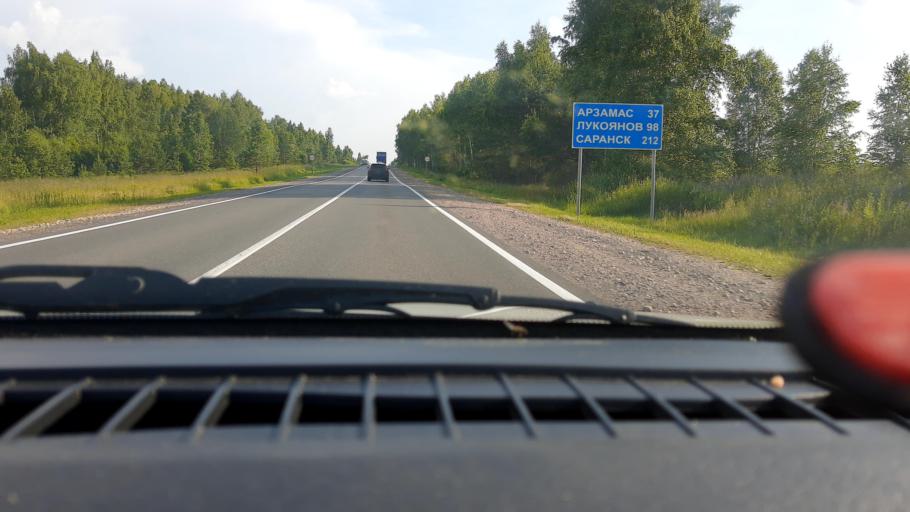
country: RU
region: Nizjnij Novgorod
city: Surovatikha
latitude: 55.7504
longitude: 43.9910
